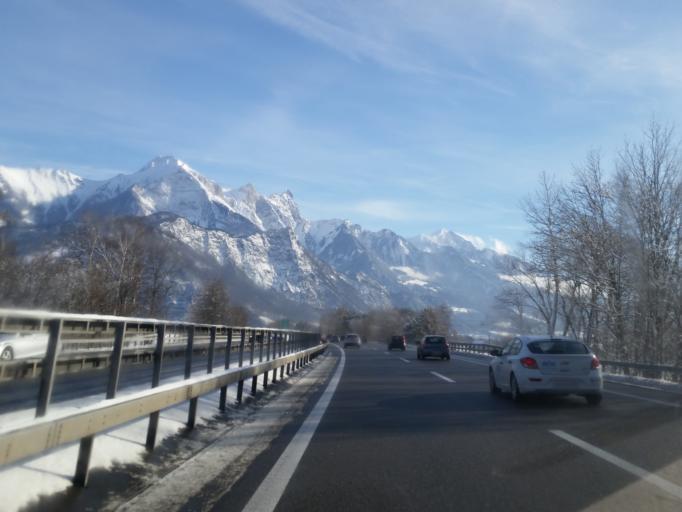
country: CH
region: Saint Gallen
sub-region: Wahlkreis Sarganserland
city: Sargans
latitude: 47.0384
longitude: 9.4476
